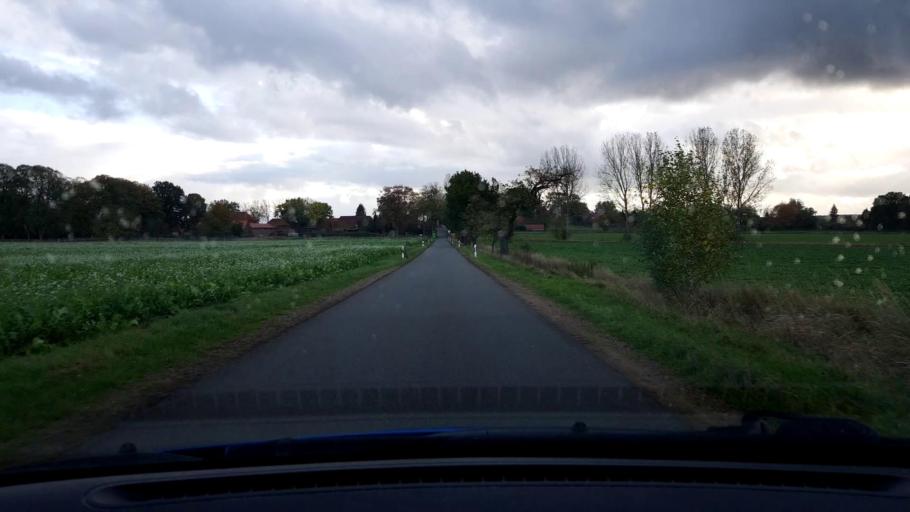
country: DE
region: Lower Saxony
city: Reinstorf
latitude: 53.2550
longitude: 10.5645
